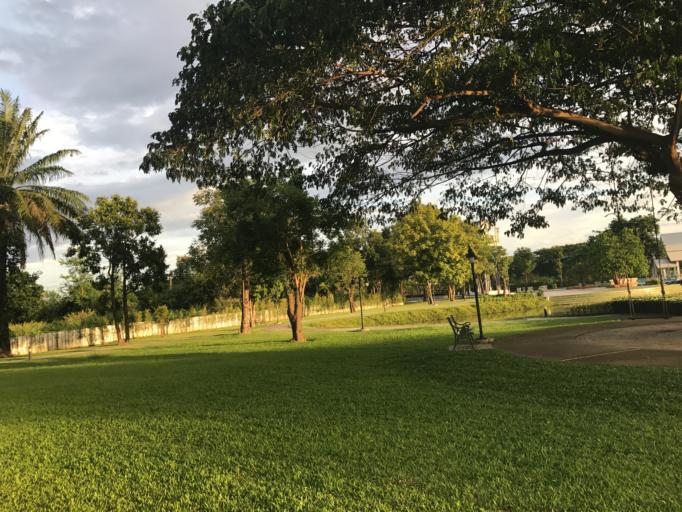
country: TH
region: Chiang Mai
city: Hang Dong
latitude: 18.7110
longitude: 98.9088
